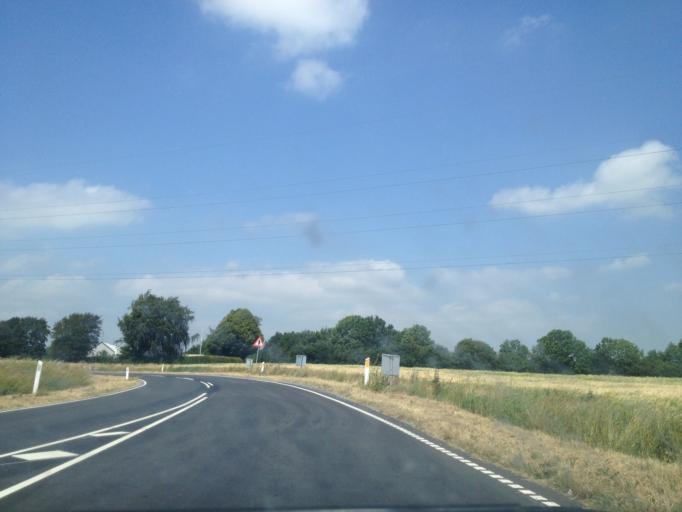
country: DK
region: South Denmark
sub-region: Haderslev Kommune
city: Vojens
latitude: 55.3355
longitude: 9.2990
